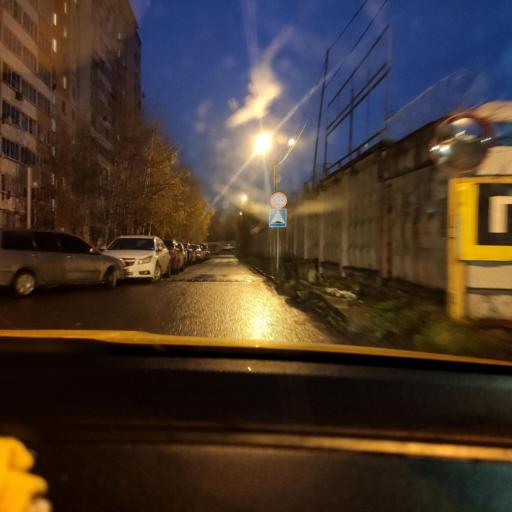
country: RU
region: Moskovskaya
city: Lesnoy Gorodok
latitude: 55.6566
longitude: 37.2040
